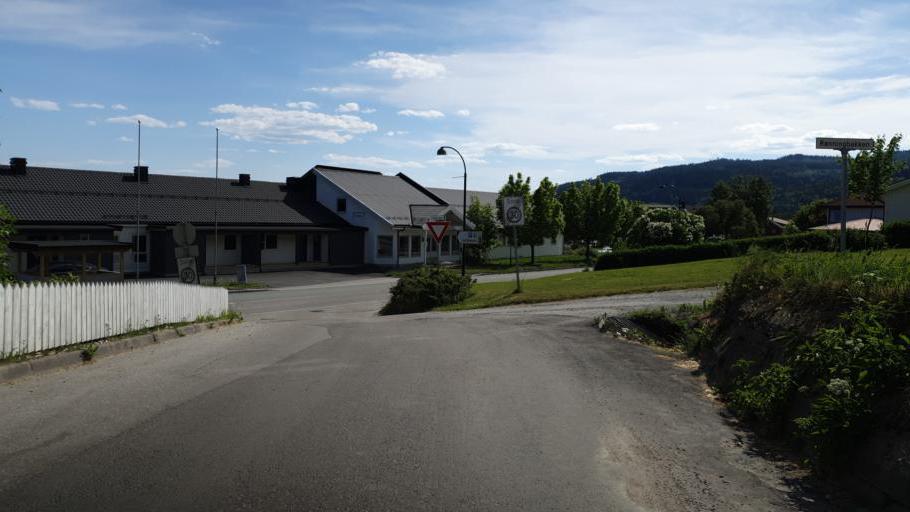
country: NO
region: Nord-Trondelag
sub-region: Leksvik
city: Leksvik
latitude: 63.6713
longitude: 10.6205
